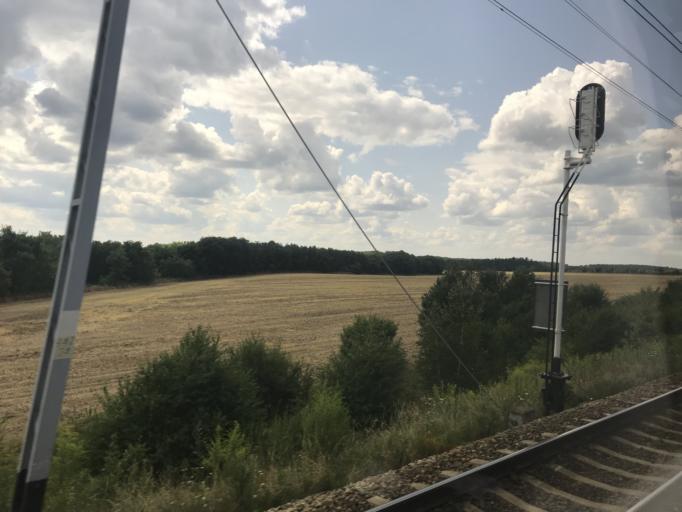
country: PL
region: Lubusz
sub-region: Powiat sulecinski
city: Torzym
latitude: 52.3238
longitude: 15.0004
